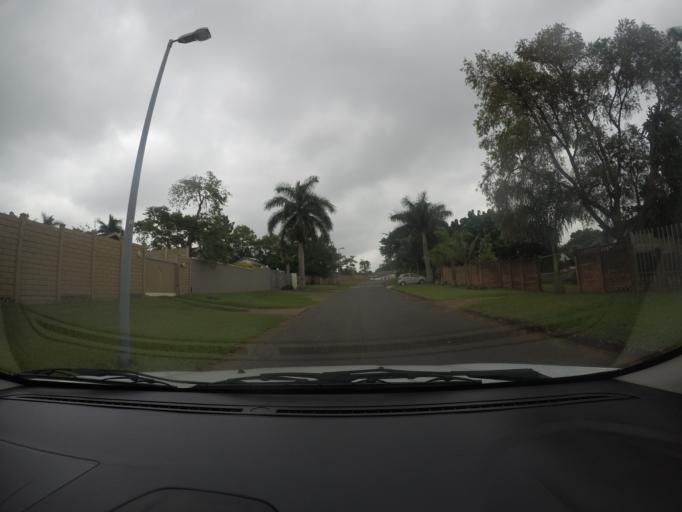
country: ZA
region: KwaZulu-Natal
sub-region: uThungulu District Municipality
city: Empangeni
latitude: -28.7636
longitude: 31.8975
